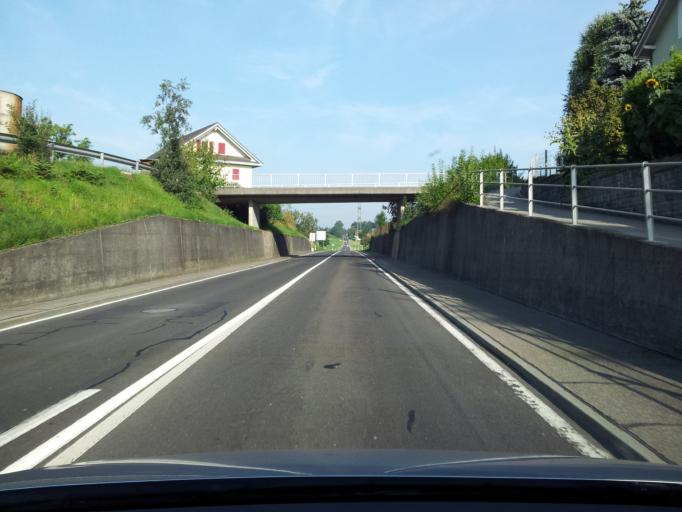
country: CH
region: Lucerne
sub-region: Hochdorf District
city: Emmen
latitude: 47.0837
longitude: 8.2441
